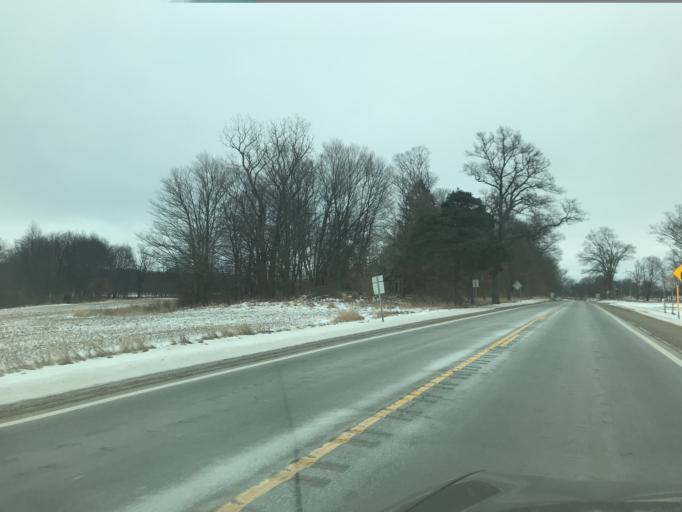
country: US
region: Michigan
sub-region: Eaton County
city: Eaton Rapids
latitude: 42.3962
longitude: -84.5941
